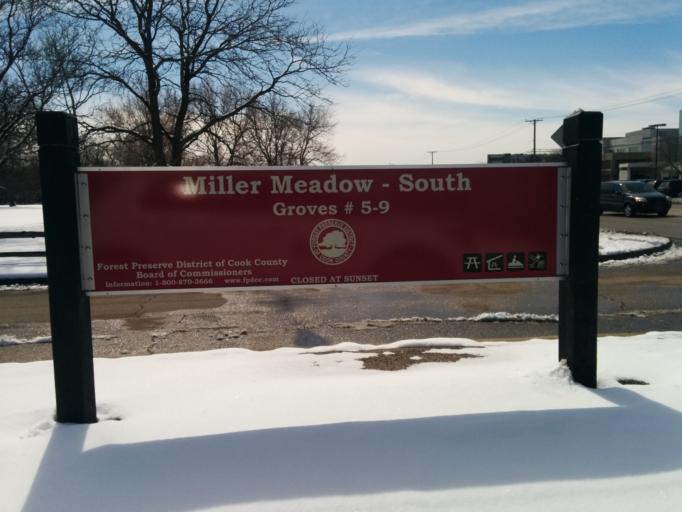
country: US
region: Illinois
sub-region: Cook County
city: North Riverside
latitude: 41.8587
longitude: -87.8330
